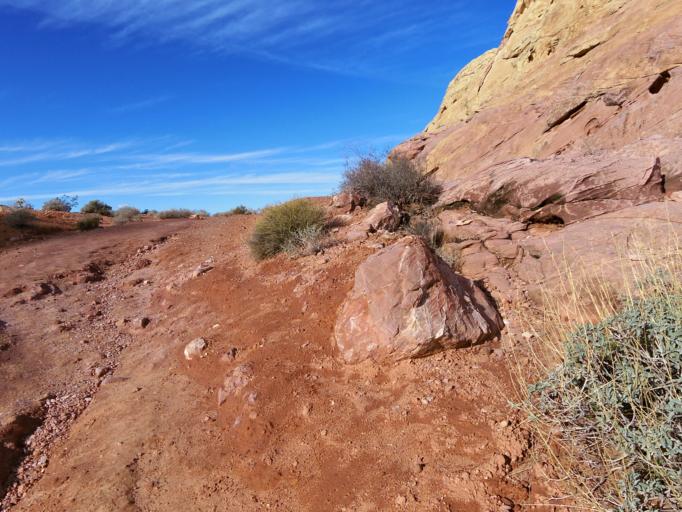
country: US
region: Nevada
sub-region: Clark County
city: Moapa Valley
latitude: 36.4848
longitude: -114.5351
